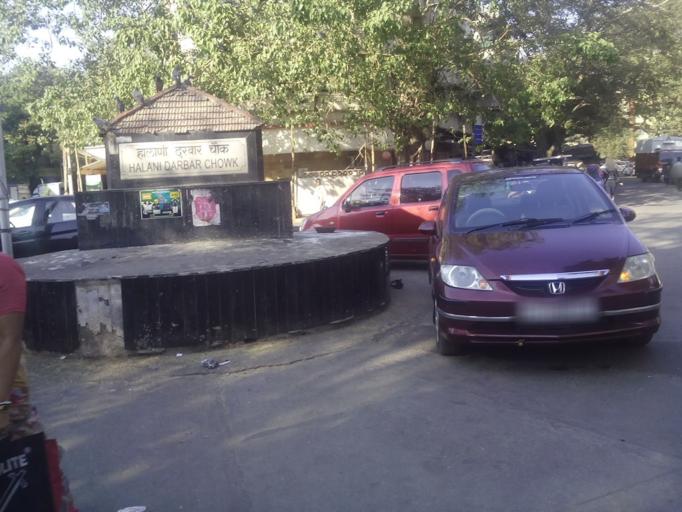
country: IN
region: Maharashtra
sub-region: Mumbai Suburban
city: Mumbai
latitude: 19.0434
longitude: 72.8609
